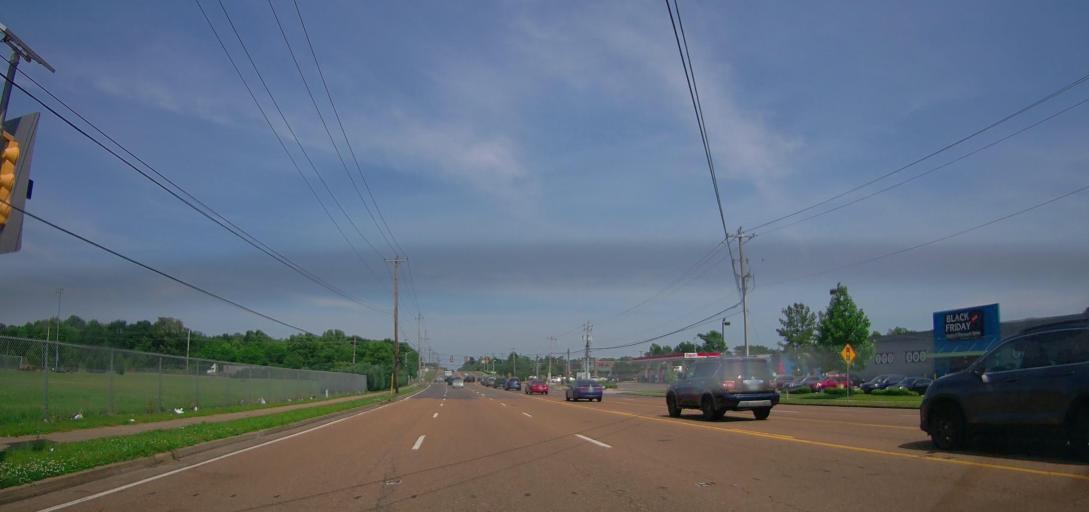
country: US
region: Mississippi
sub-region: De Soto County
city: Olive Branch
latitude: 35.0206
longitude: -89.7979
